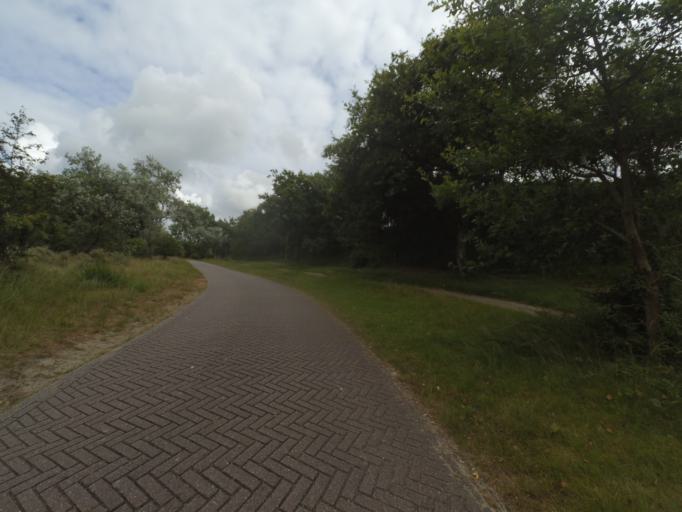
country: NL
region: South Holland
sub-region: Gemeente Den Haag
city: The Hague
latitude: 52.1259
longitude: 4.3311
